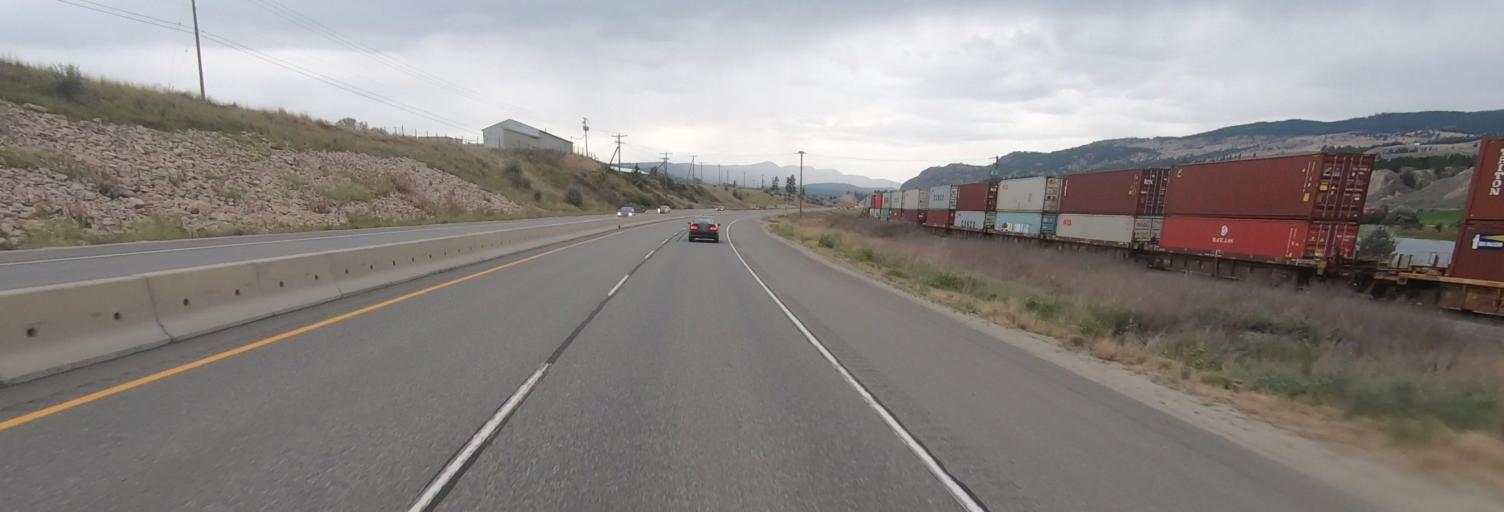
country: CA
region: British Columbia
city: Chase
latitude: 50.6746
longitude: -119.8352
